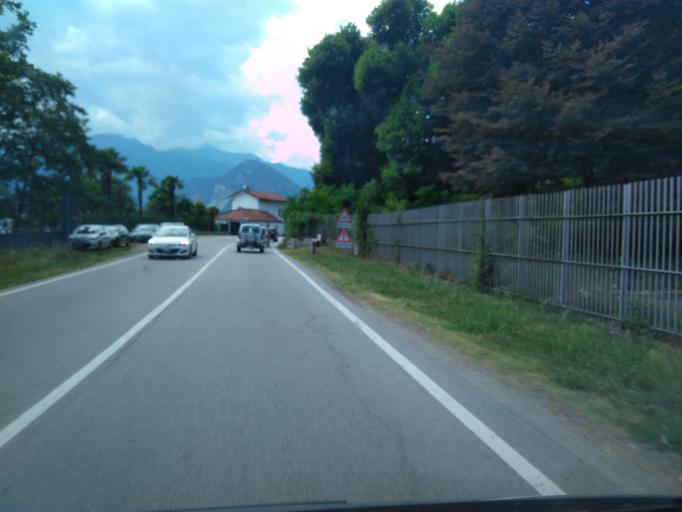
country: IT
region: Piedmont
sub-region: Provincia Verbano-Cusio-Ossola
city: Santino
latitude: 45.9378
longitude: 8.5177
